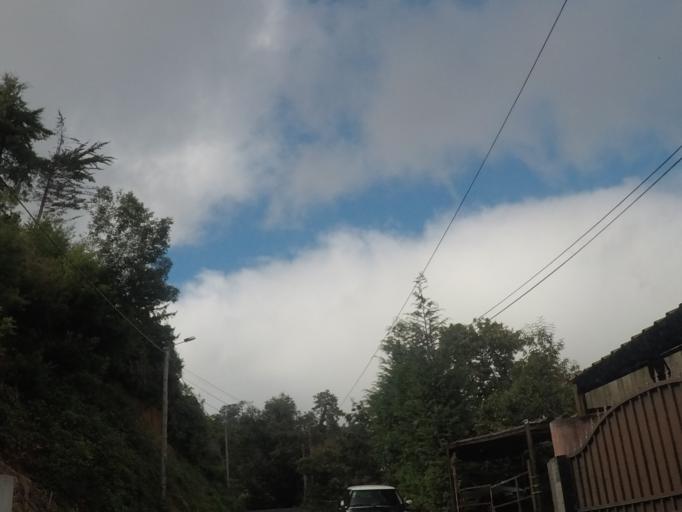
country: PT
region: Madeira
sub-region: Santa Cruz
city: Camacha
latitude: 32.6801
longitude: -16.8540
